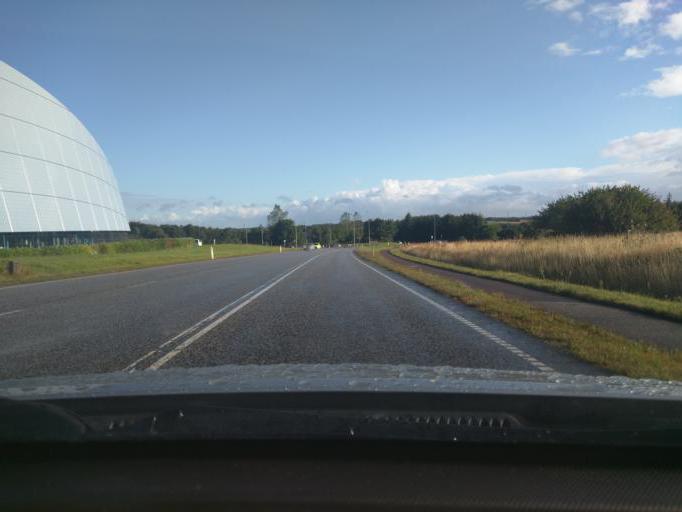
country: DK
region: Central Jutland
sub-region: Viborg Kommune
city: Viborg
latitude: 56.4729
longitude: 9.4159
